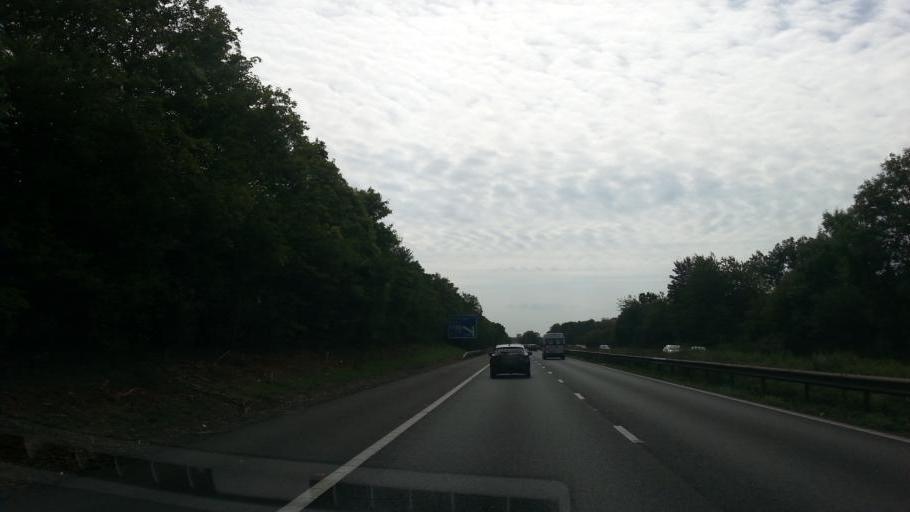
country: GB
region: England
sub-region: Hertfordshire
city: Stevenage
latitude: 51.8981
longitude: -0.2166
